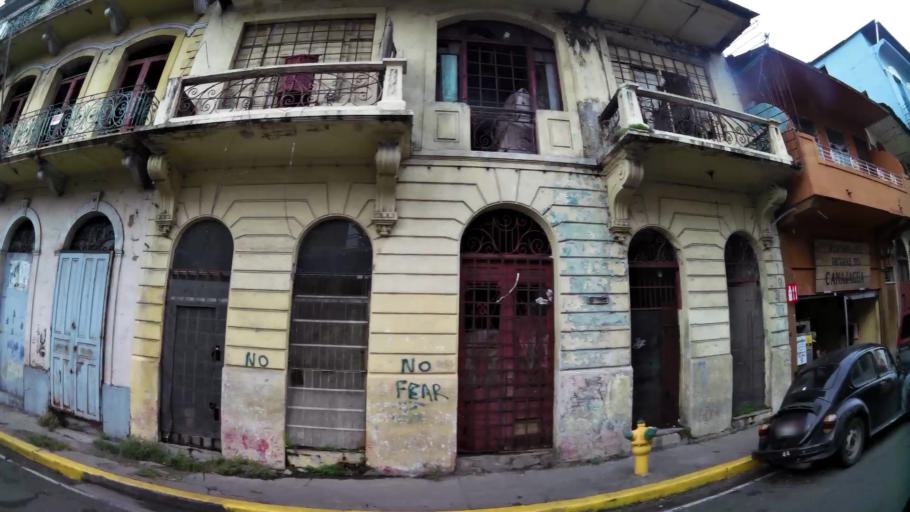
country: PA
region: Panama
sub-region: Distrito de Panama
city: Ancon
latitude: 8.9537
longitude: -79.5378
